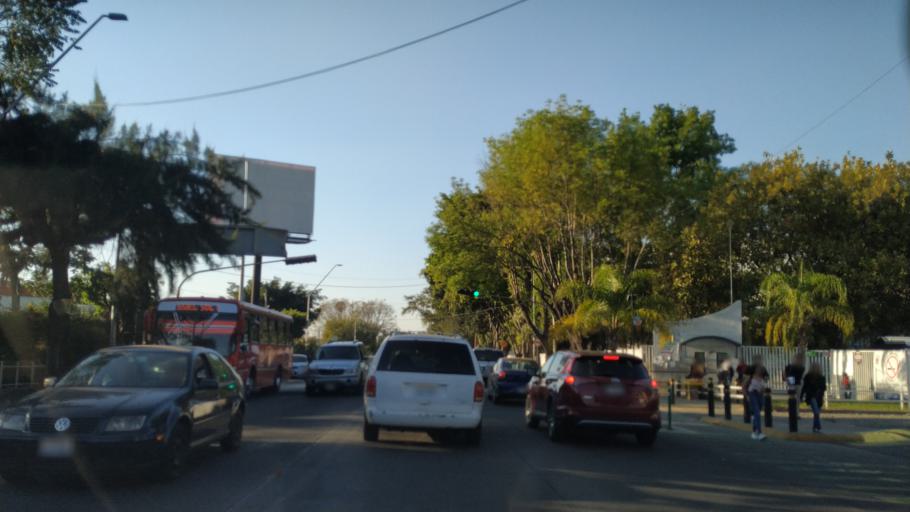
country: MX
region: Jalisco
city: Tlaquepaque
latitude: 20.6542
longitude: -103.3265
